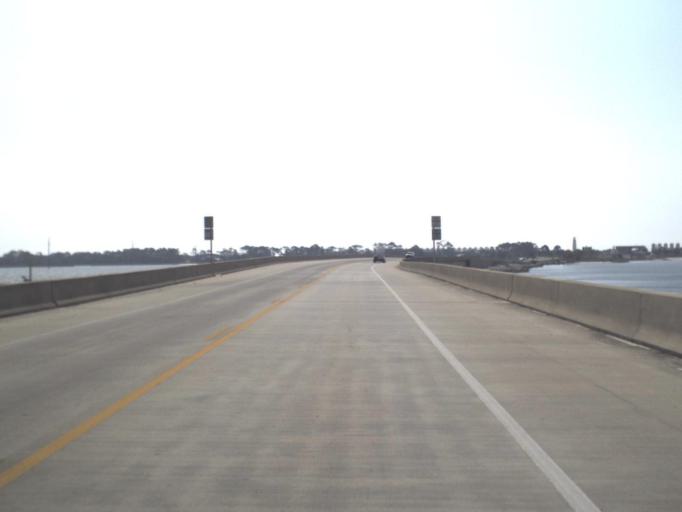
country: US
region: Florida
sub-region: Franklin County
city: Eastpoint
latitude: 29.6732
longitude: -84.8694
